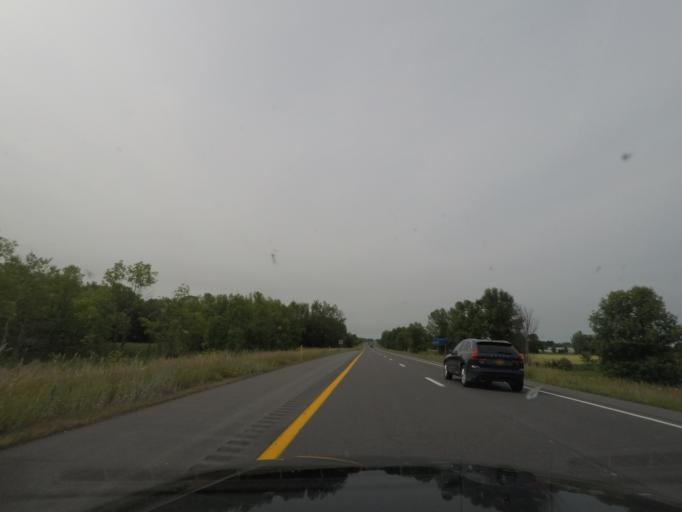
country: US
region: New York
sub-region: Clinton County
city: Cumberland Head
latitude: 44.7729
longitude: -73.4344
